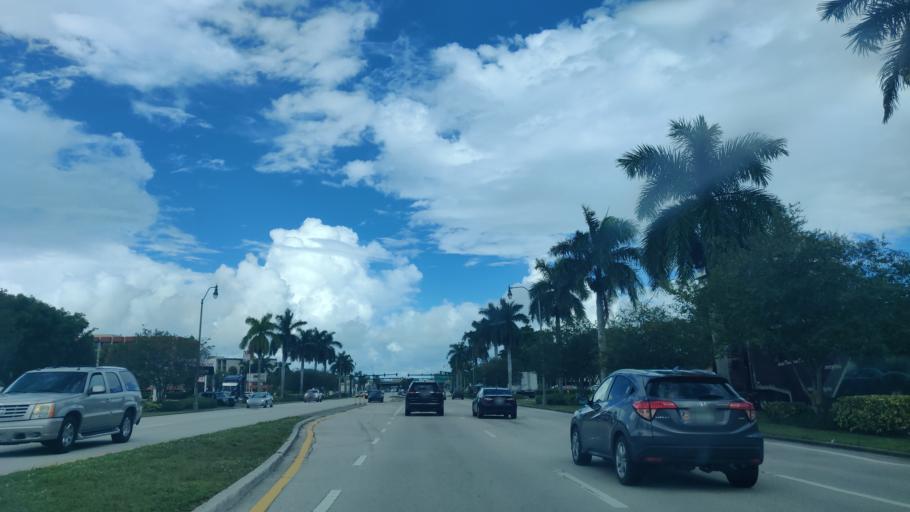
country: US
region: Florida
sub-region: Palm Beach County
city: Schall Circle
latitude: 26.7144
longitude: -80.0936
